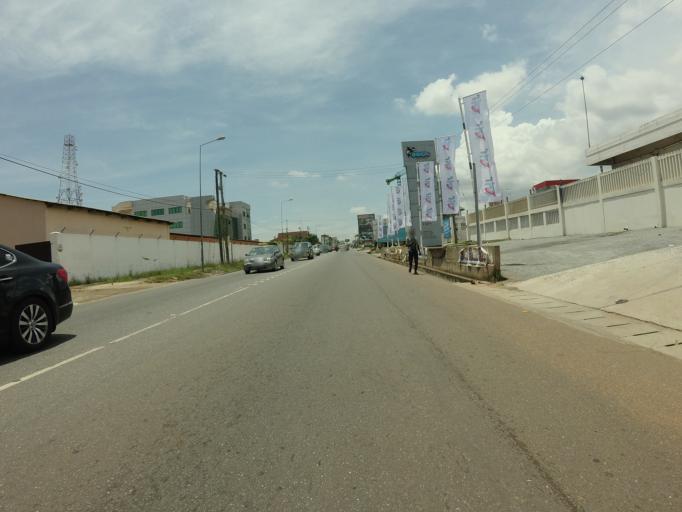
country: GH
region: Greater Accra
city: Medina Estates
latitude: 5.6289
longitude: -0.1479
